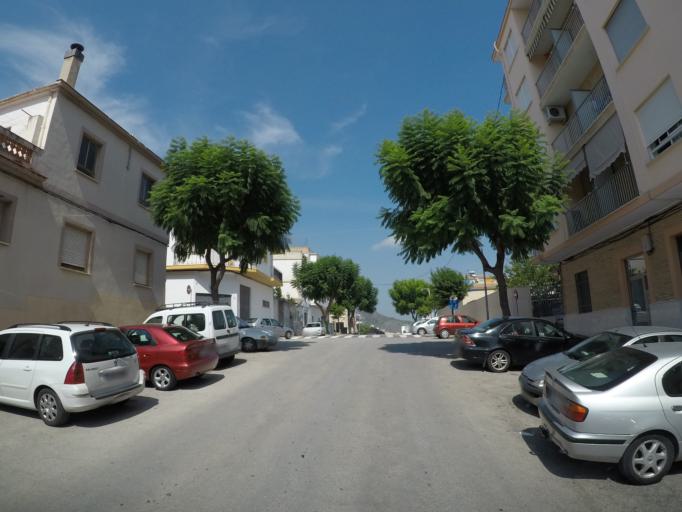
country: ES
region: Valencia
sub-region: Provincia de Alicante
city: Pego
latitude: 38.8414
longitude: -0.1129
